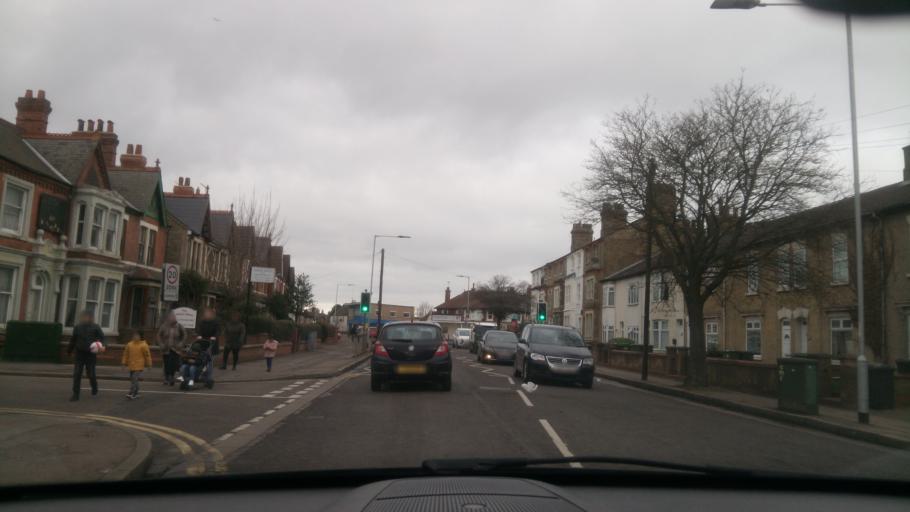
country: GB
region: England
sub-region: Peterborough
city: Peterborough
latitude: 52.5819
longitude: -0.2441
